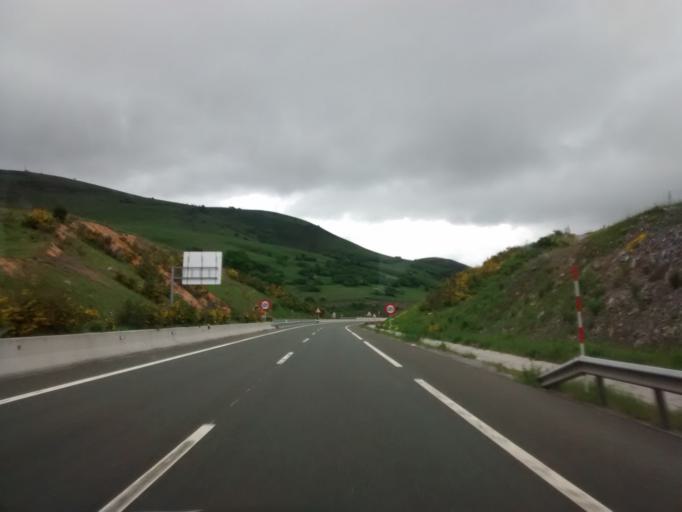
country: ES
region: Cantabria
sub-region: Provincia de Cantabria
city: Pesquera
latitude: 43.0770
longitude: -4.0859
